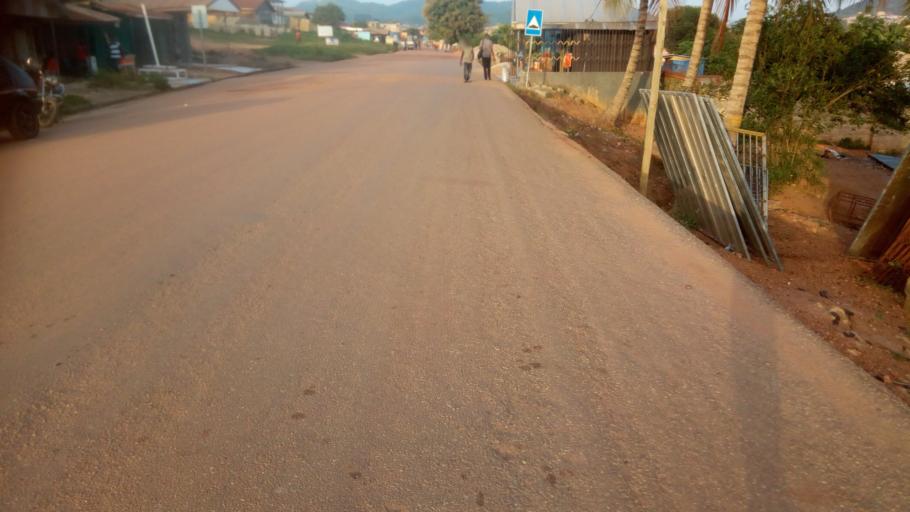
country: GH
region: Ashanti
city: Obuasi
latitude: 6.2124
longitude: -1.6934
